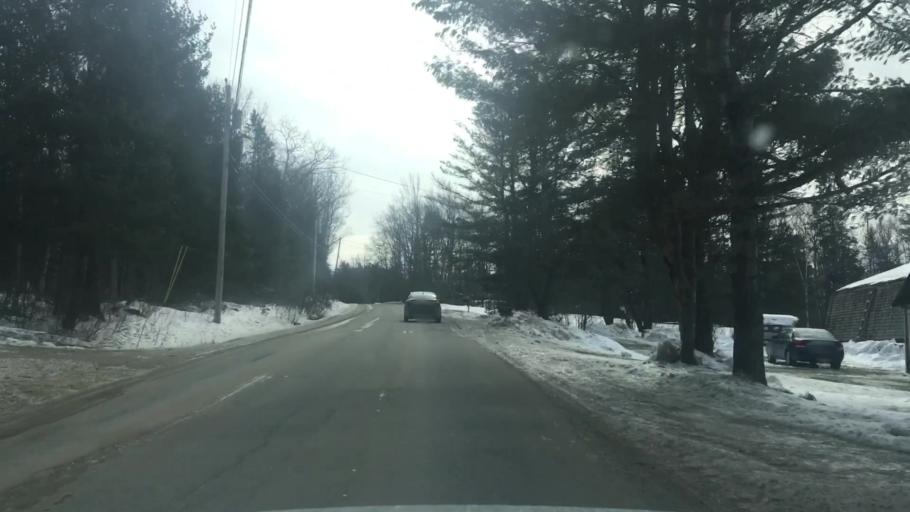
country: US
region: Maine
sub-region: Hancock County
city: Orland
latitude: 44.5862
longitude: -68.7259
